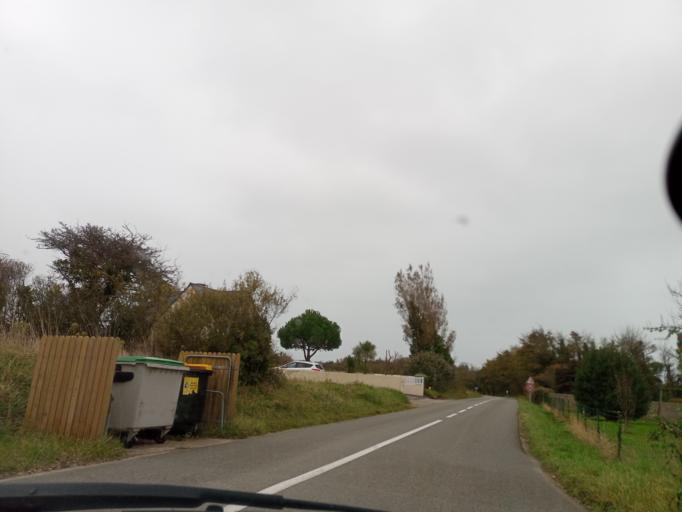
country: FR
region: Brittany
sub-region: Departement du Finistere
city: Esquibien
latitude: 48.0197
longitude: -4.5638
